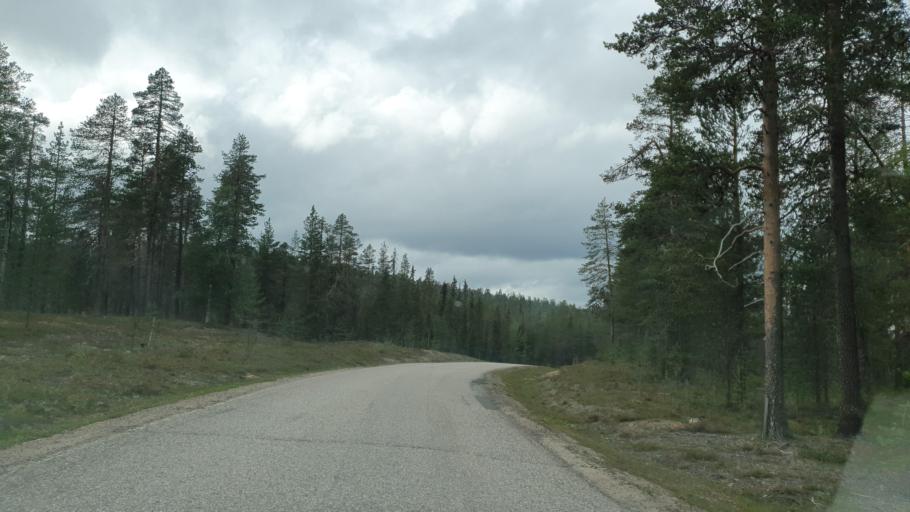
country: FI
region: Lapland
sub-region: Tunturi-Lappi
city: Kolari
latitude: 67.5224
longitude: 24.1708
